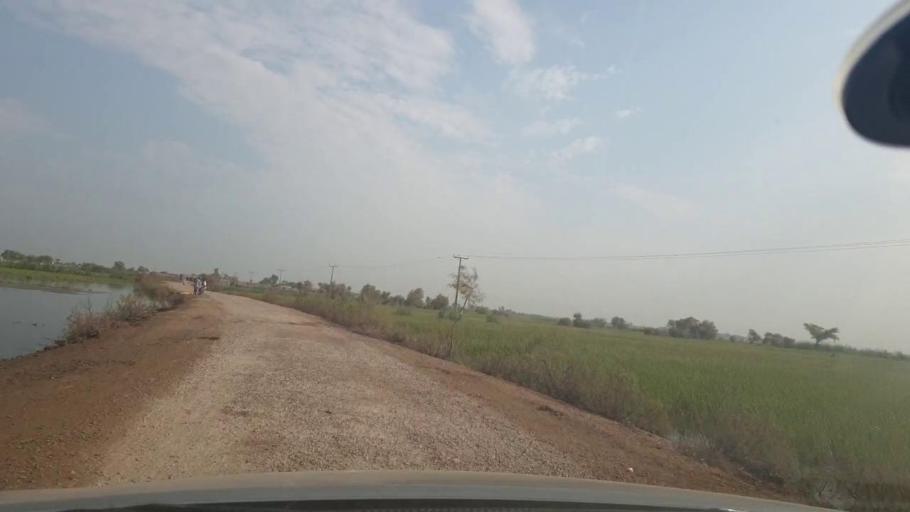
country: PK
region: Balochistan
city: Mehrabpur
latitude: 28.0696
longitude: 68.2109
